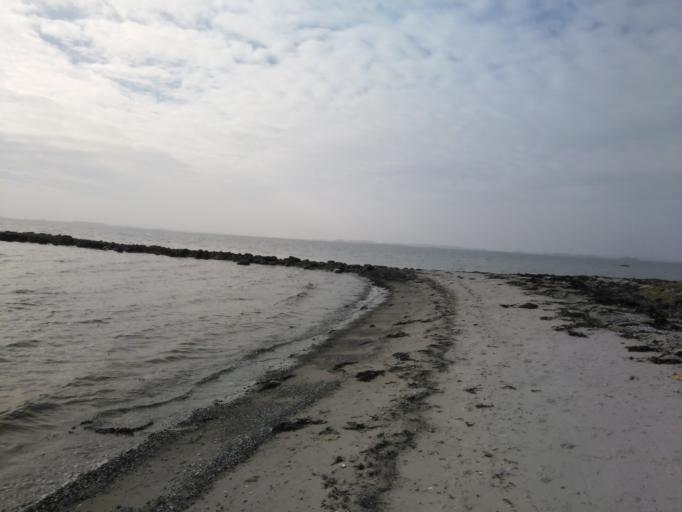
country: DK
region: Central Jutland
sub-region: Odder Kommune
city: Odder
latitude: 55.8460
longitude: 10.1599
